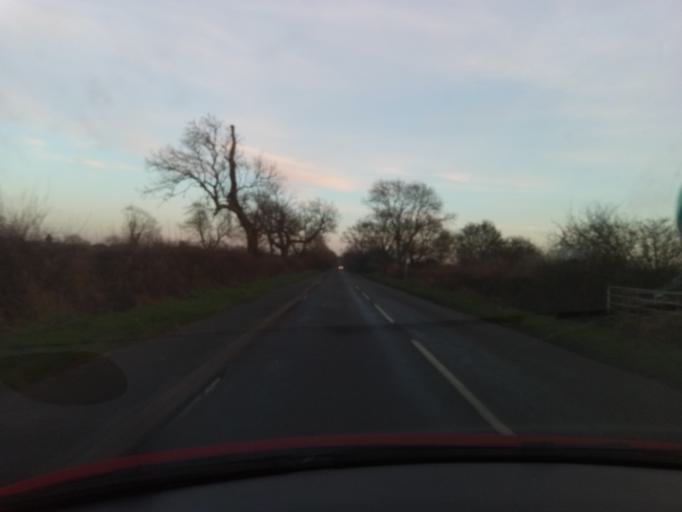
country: GB
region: England
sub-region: Leicestershire
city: Sileby
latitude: 52.7312
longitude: -1.1258
